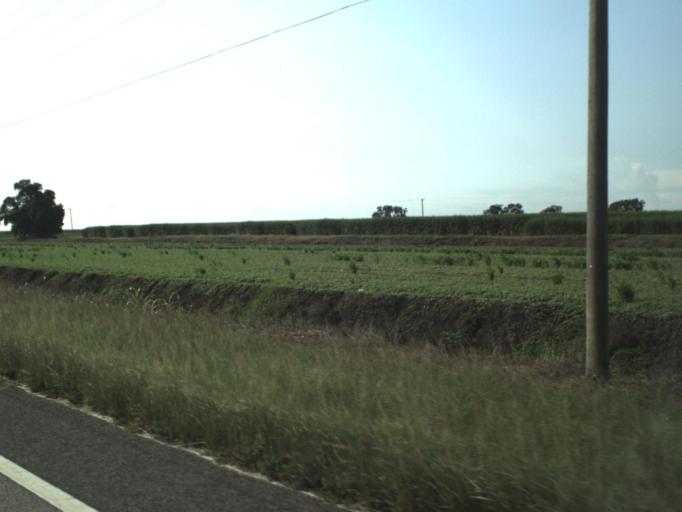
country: US
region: Florida
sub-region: Palm Beach County
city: South Bay
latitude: 26.6849
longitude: -80.7565
